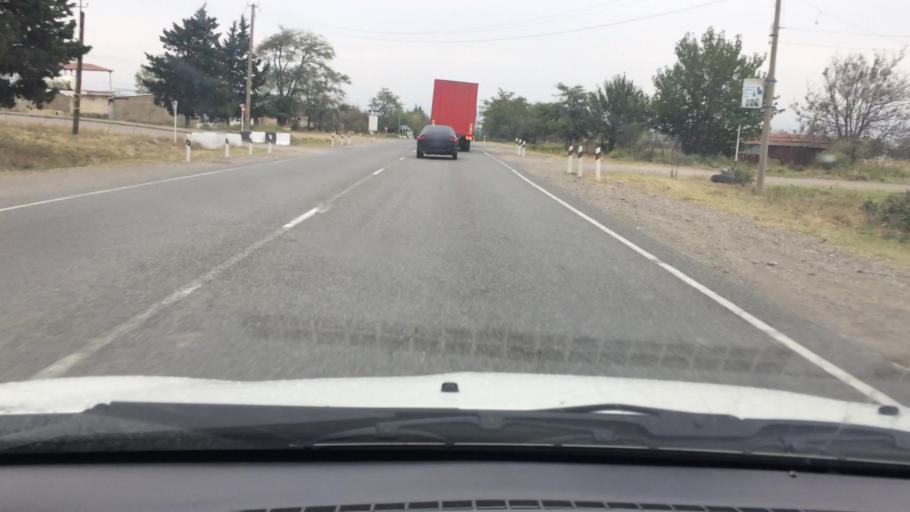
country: GE
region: T'bilisi
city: Tbilisi
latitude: 41.6430
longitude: 44.8542
